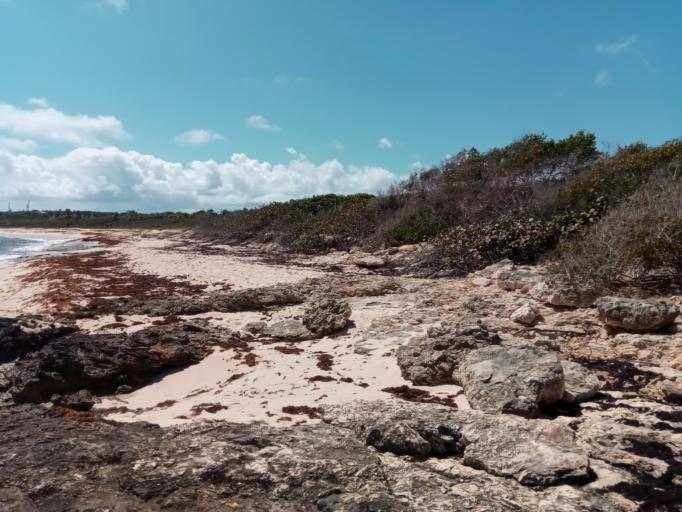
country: GP
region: Guadeloupe
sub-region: Guadeloupe
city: Saint-Francois
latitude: 16.2616
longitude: -61.2181
